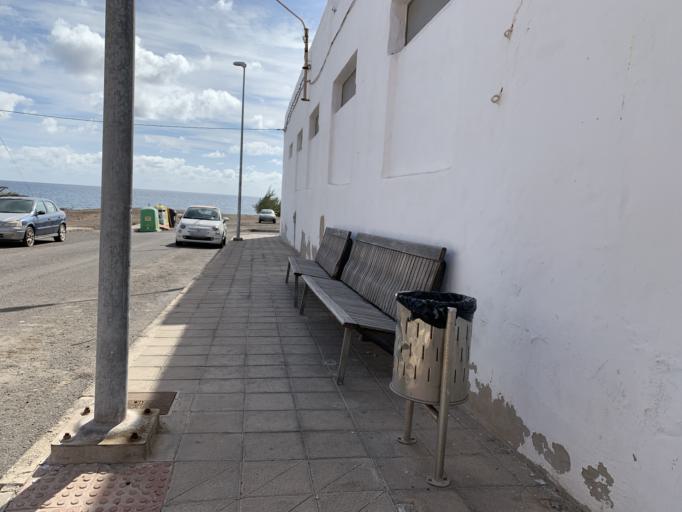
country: ES
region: Canary Islands
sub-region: Provincia de Las Palmas
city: Puerto del Rosario
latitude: 28.5020
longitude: -13.8484
